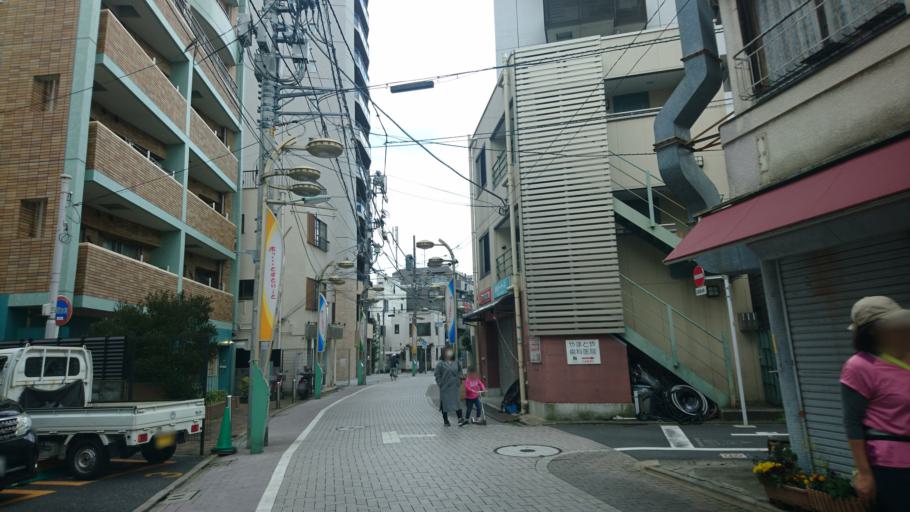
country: JP
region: Tokyo
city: Tokyo
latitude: 35.6071
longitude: 139.7178
